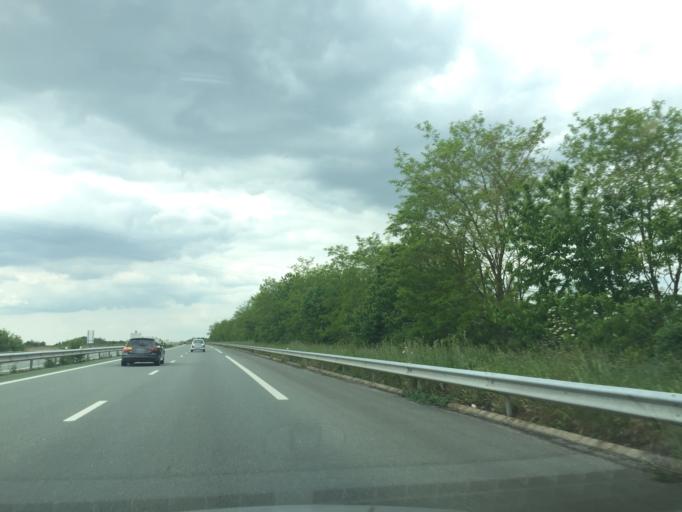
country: FR
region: Poitou-Charentes
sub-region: Departement des Deux-Sevres
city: Villiers-en-Plaine
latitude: 46.4297
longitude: -0.5128
